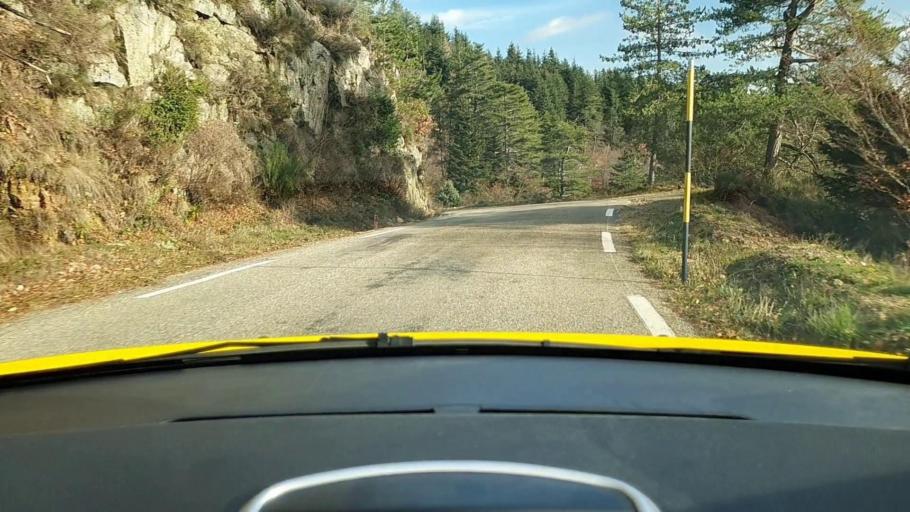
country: FR
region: Languedoc-Roussillon
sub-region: Departement du Gard
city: Branoux-les-Taillades
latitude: 44.3529
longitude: 3.9272
